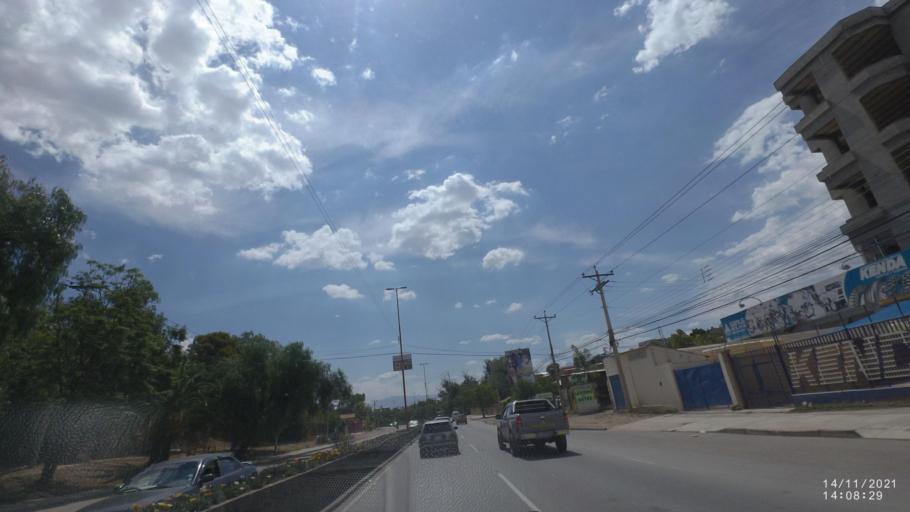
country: BO
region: Cochabamba
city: Cochabamba
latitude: -17.3745
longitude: -66.1332
